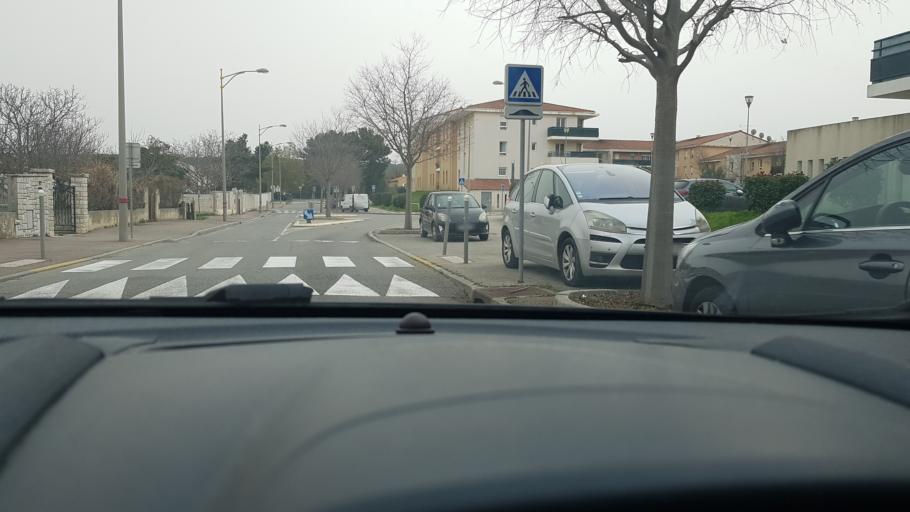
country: FR
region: Provence-Alpes-Cote d'Azur
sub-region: Departement des Bouches-du-Rhone
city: Gardanne
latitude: 43.4444
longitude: 5.4705
